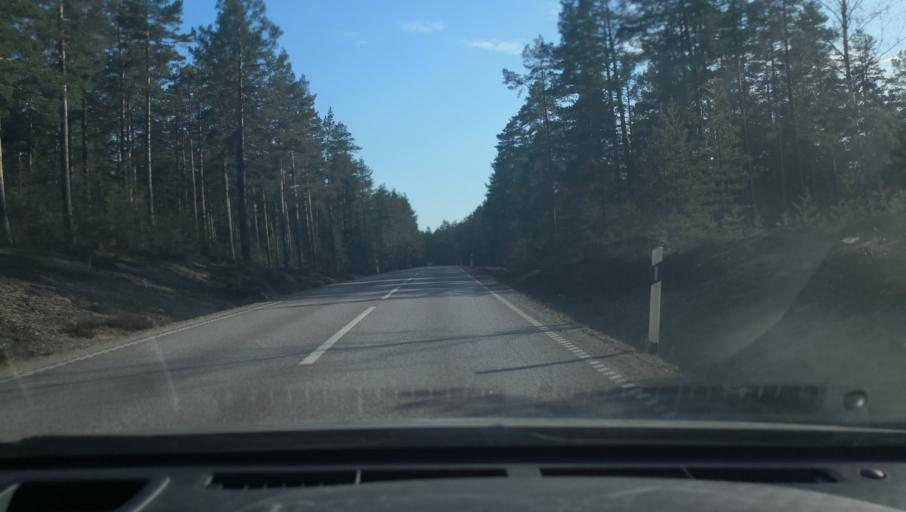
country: SE
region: Uppsala
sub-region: Heby Kommun
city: Tarnsjo
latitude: 60.1053
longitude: 16.8845
